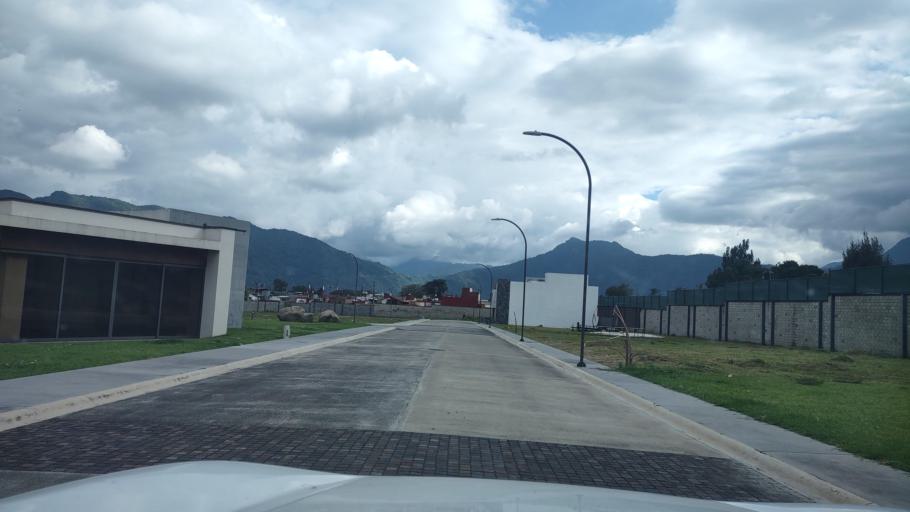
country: MX
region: Veracruz
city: Orizaba
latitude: 18.8428
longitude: -97.0889
